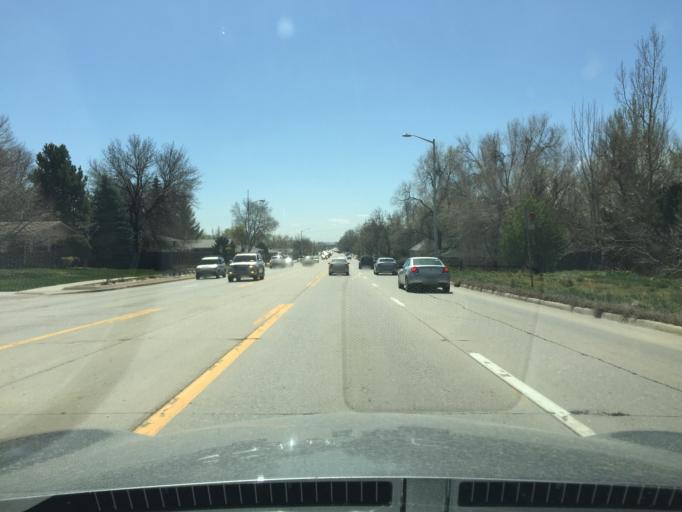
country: US
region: Colorado
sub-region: Boulder County
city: Longmont
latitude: 40.1701
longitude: -105.1309
